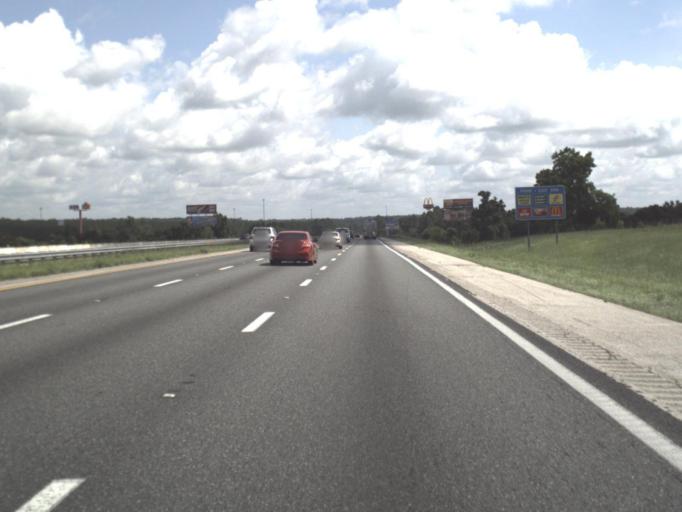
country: US
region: Florida
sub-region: Alachua County
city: High Springs
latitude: 29.7963
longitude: -82.5145
